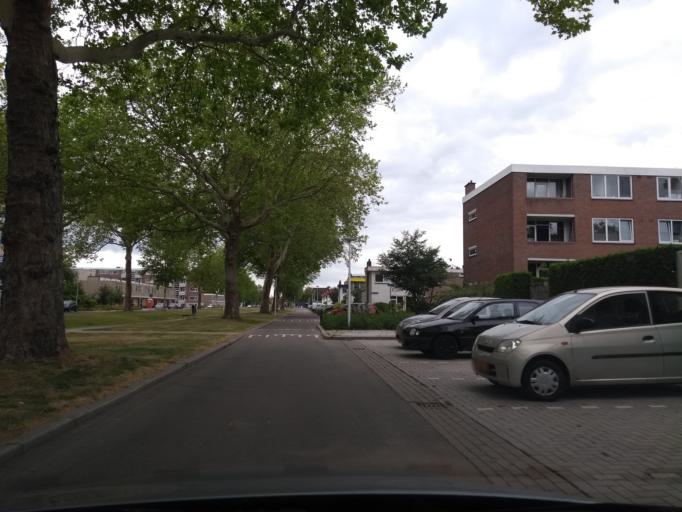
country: NL
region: Overijssel
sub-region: Gemeente Hengelo
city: Hengelo
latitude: 52.2689
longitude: 6.8144
